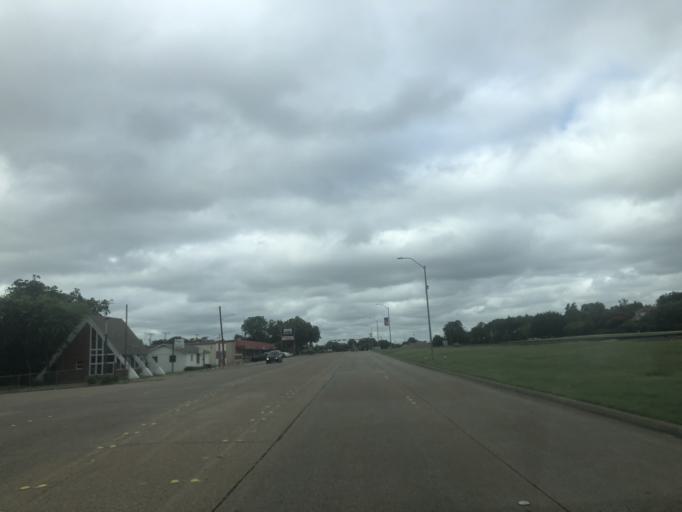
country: US
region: Texas
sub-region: Dallas County
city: Duncanville
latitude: 32.6572
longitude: -96.9076
